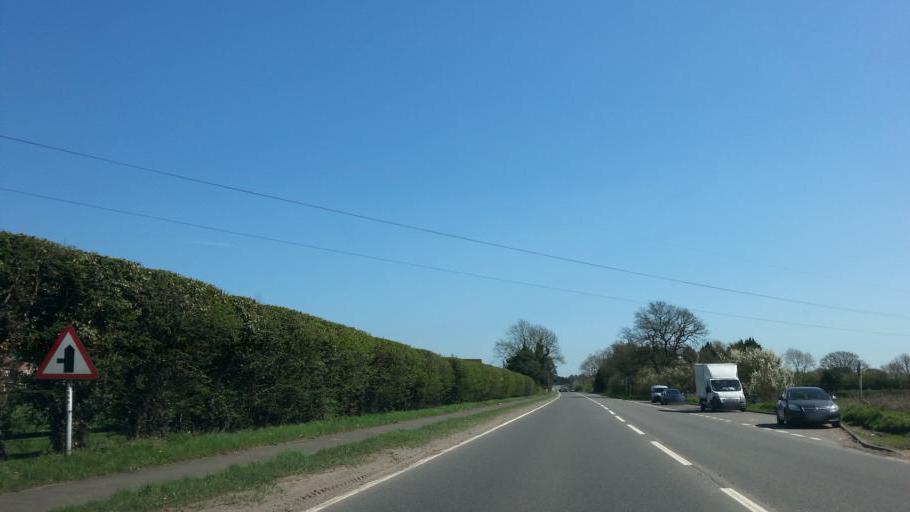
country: GB
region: England
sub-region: Staffordshire
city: Penkridge
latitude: 52.6911
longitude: -2.1179
